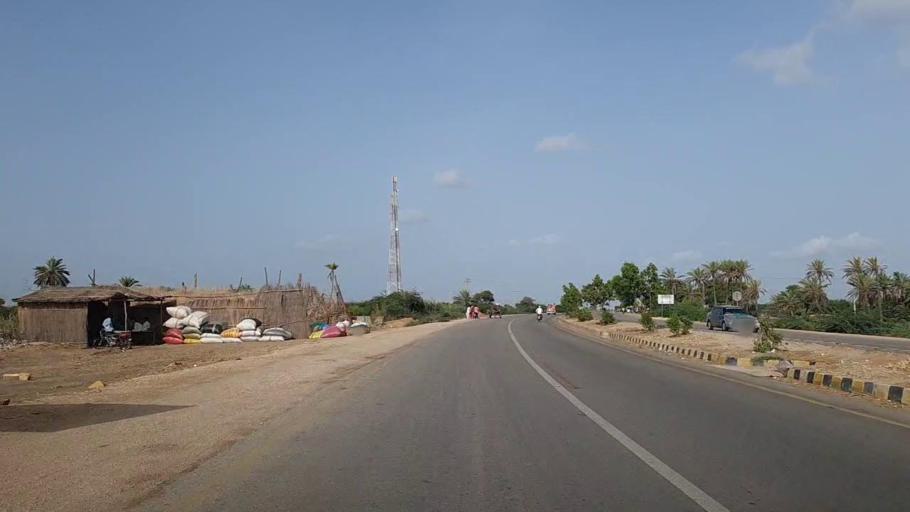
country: PK
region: Sindh
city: Thatta
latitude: 24.7429
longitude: 67.7714
